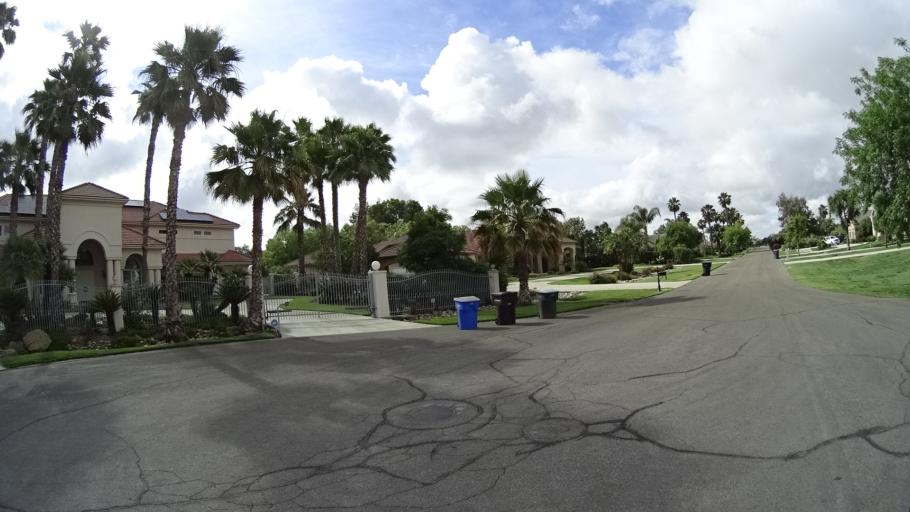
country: US
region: California
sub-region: Kings County
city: Lucerne
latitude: 36.3533
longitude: -119.6758
